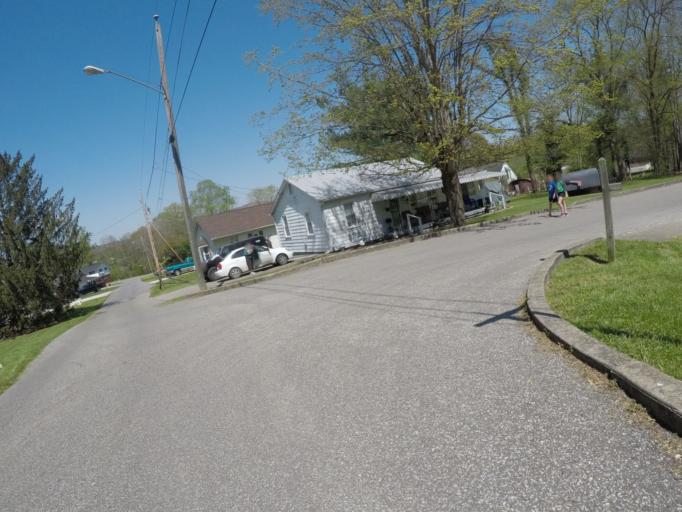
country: US
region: West Virginia
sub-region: Cabell County
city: Barboursville
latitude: 38.4026
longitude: -82.3006
